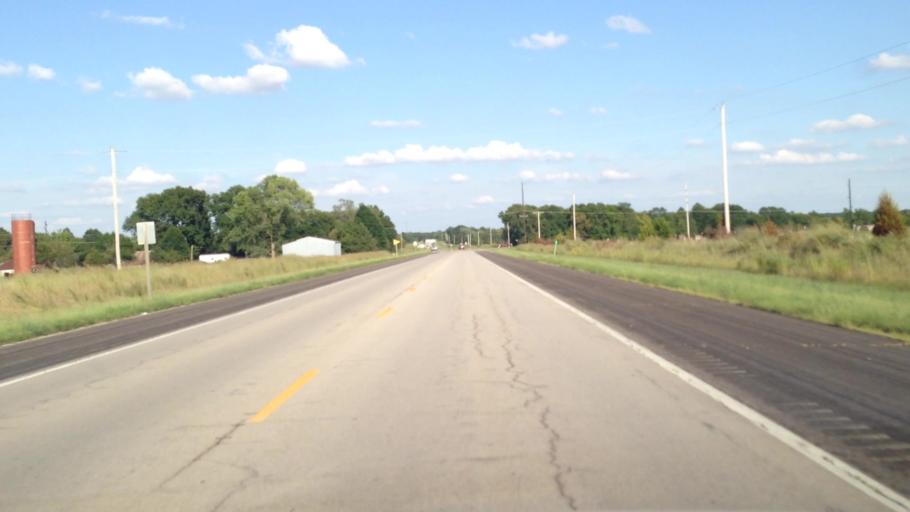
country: US
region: Kansas
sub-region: Crawford County
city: Frontenac
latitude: 37.4689
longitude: -94.6346
